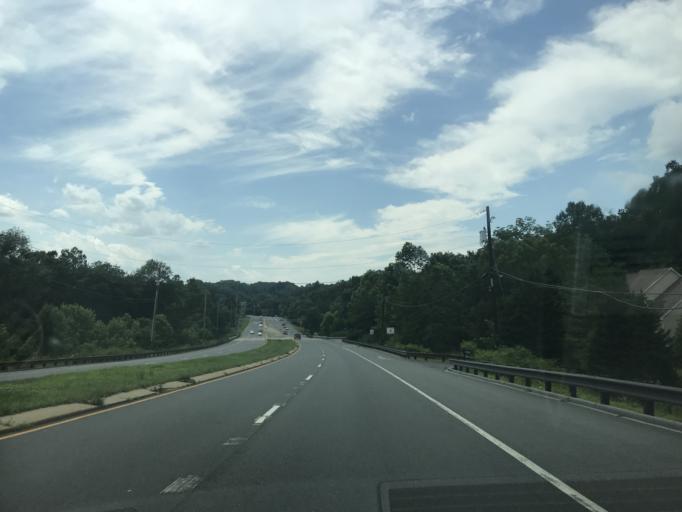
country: US
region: Delaware
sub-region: New Castle County
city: Greenville
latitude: 39.7632
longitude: -75.6338
